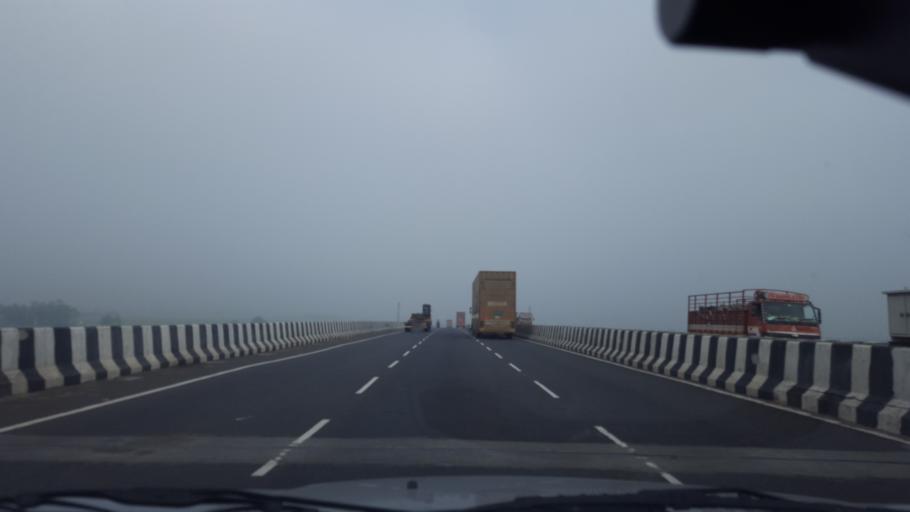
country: IN
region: Andhra Pradesh
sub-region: Prakasam
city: Ongole
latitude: 15.5161
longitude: 80.0703
